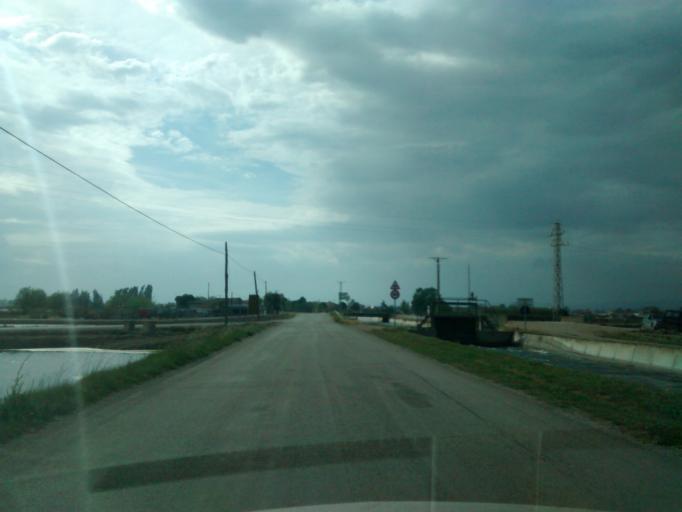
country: ES
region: Catalonia
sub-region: Provincia de Tarragona
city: Deltebre
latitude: 40.7018
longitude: 0.7417
